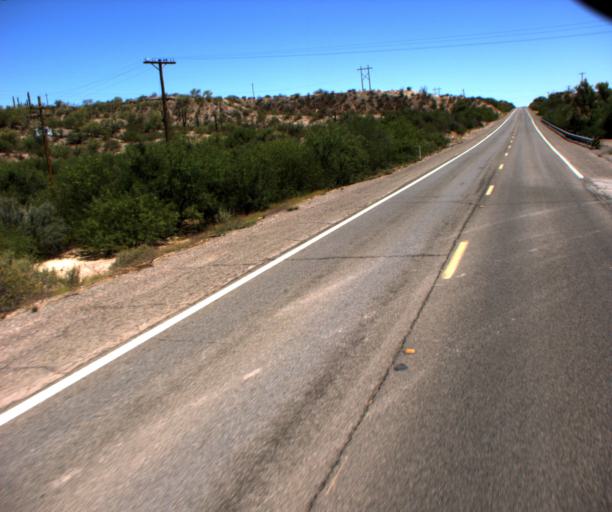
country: US
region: Arizona
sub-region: Pinal County
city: Mammoth
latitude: 32.8752
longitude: -110.7117
